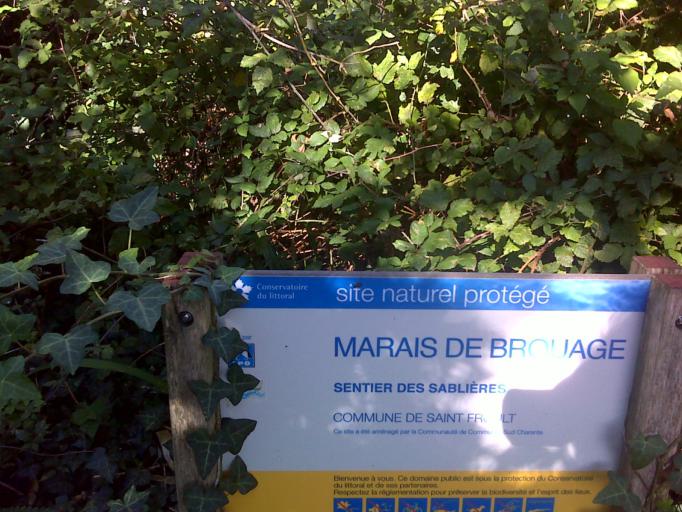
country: FR
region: Poitou-Charentes
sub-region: Departement de la Charente-Maritime
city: Port-des-Barques
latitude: 45.8980
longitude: -1.0686
